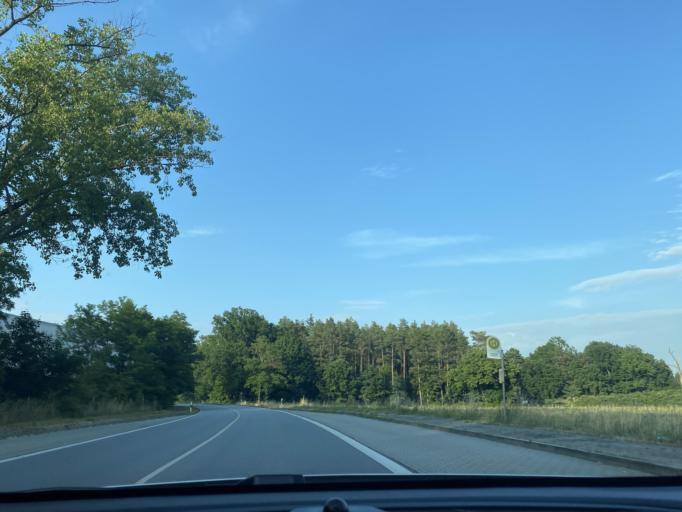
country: DE
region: Saxony
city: Niesky
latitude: 51.2695
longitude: 14.8132
